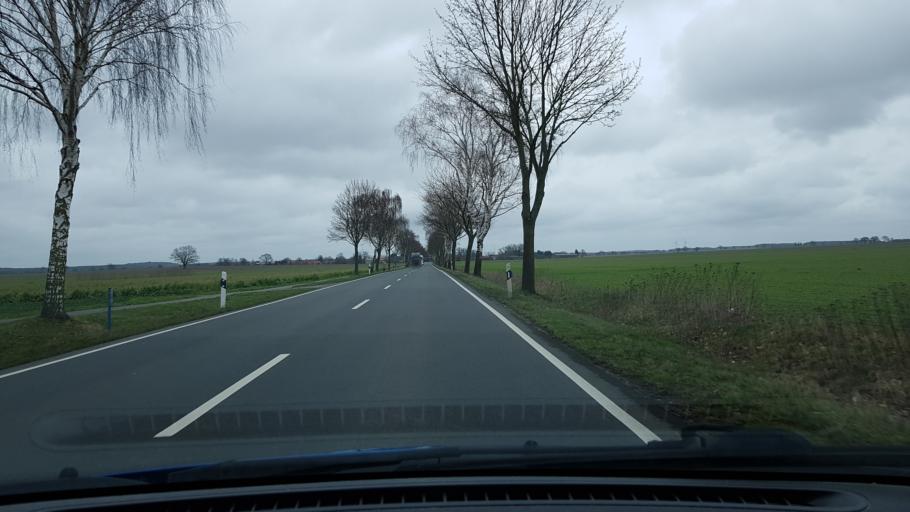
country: DE
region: Lower Saxony
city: Ratzlingen
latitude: 52.9903
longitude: 10.6388
